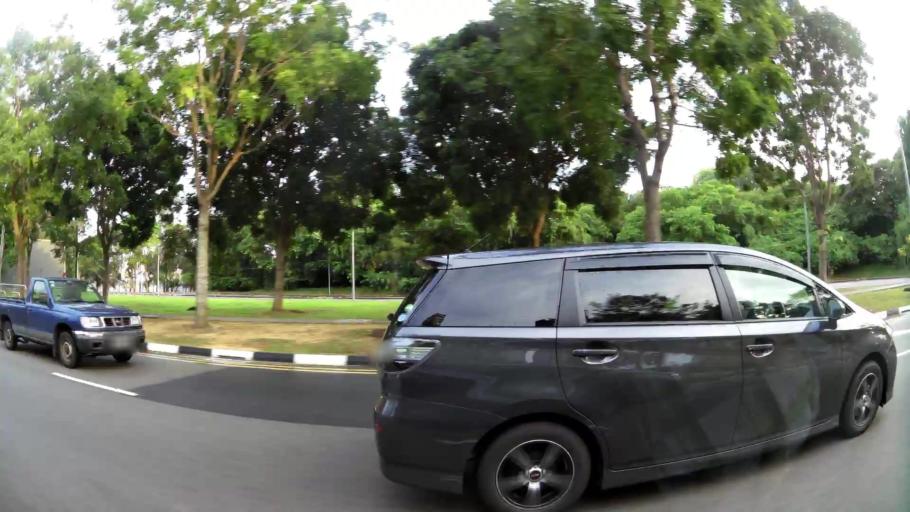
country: SG
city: Singapore
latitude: 1.2994
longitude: 103.8632
